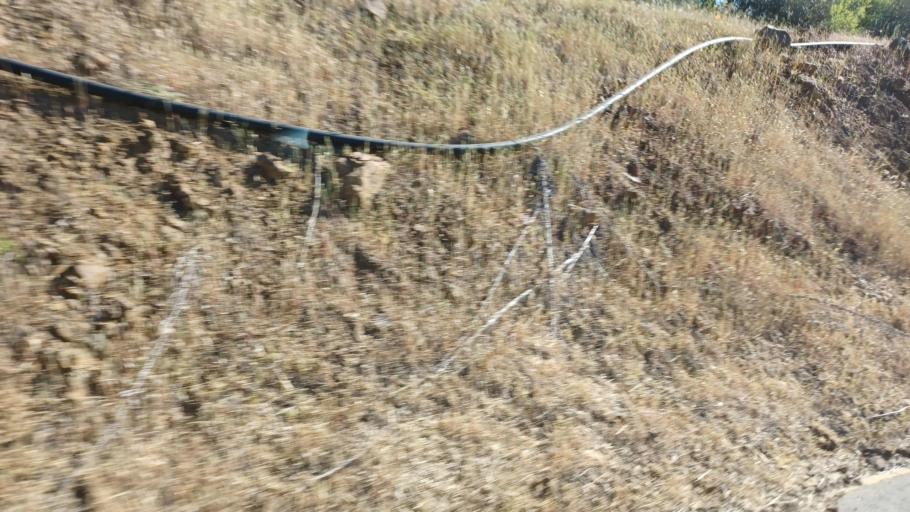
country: CY
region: Lefkosia
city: Peristerona
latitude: 35.0271
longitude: 33.0446
